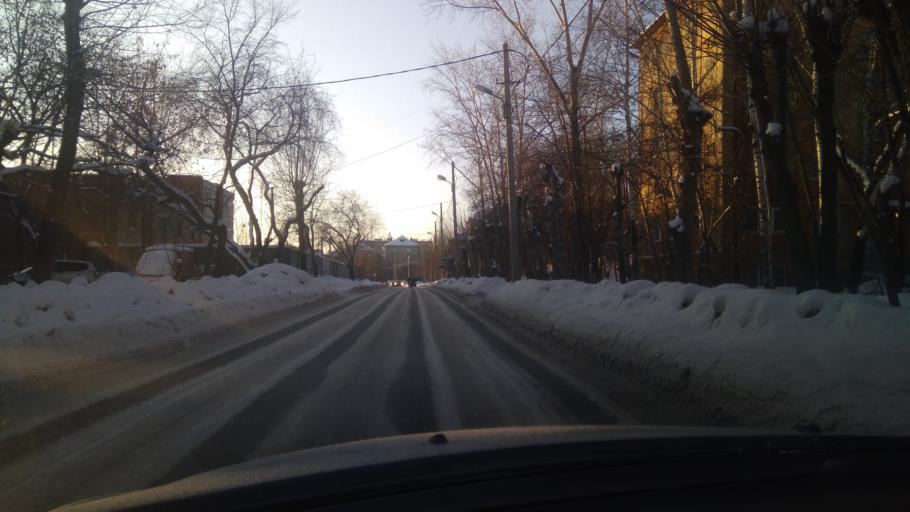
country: RU
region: Sverdlovsk
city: Yekaterinburg
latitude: 56.8836
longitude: 60.5759
